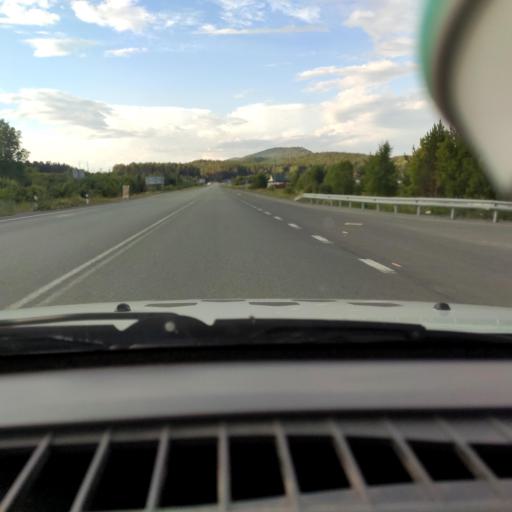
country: RU
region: Chelyabinsk
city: Turgoyak
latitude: 55.2248
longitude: 60.1872
